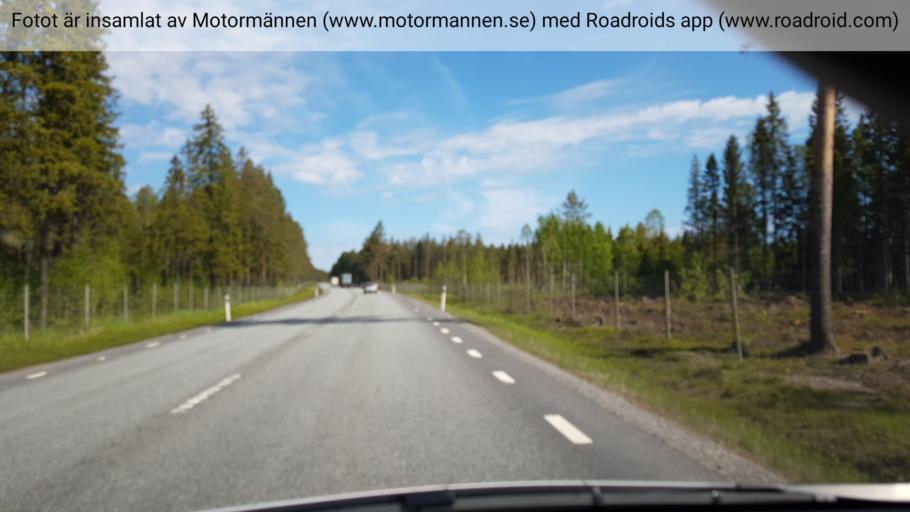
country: SE
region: Vaesterbotten
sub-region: Skelleftea Kommun
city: Burea
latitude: 64.5212
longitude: 21.2588
